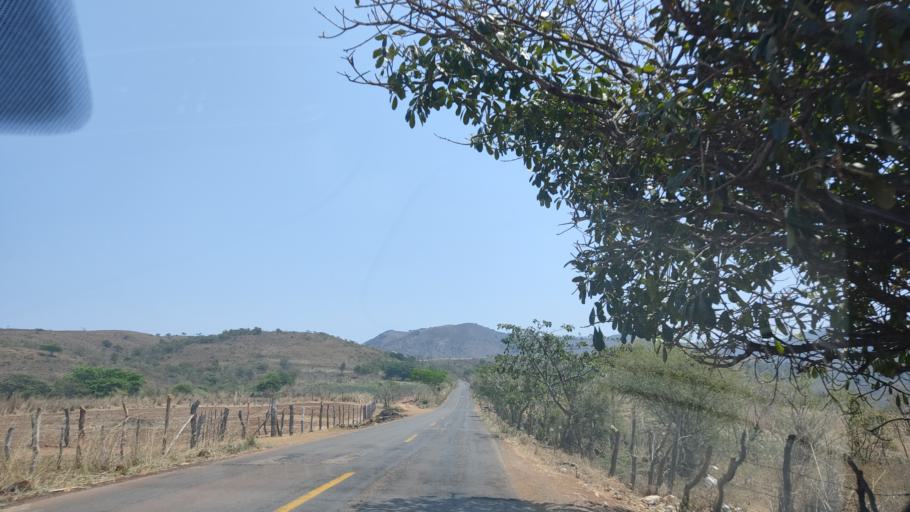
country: MX
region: Nayarit
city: Puga
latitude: 21.5790
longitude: -104.7708
